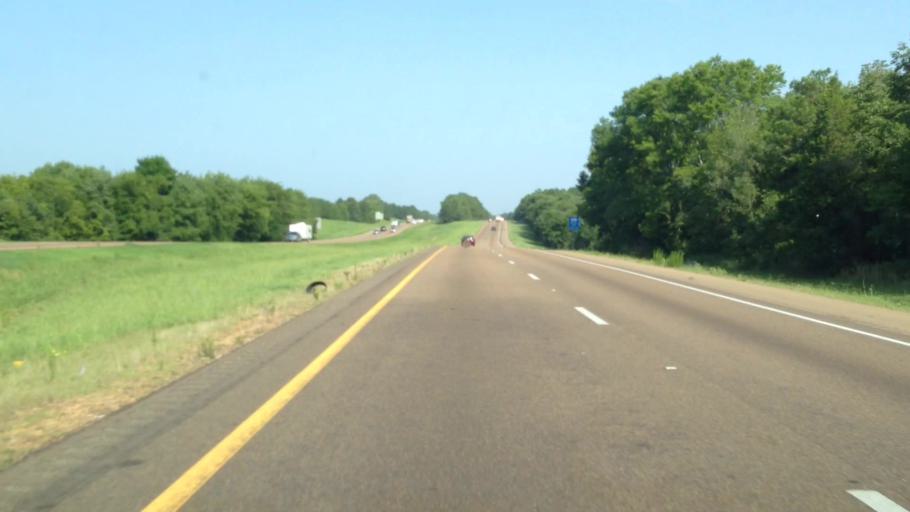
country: US
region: Mississippi
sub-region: Hinds County
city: Clinton
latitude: 32.3046
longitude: -90.2870
